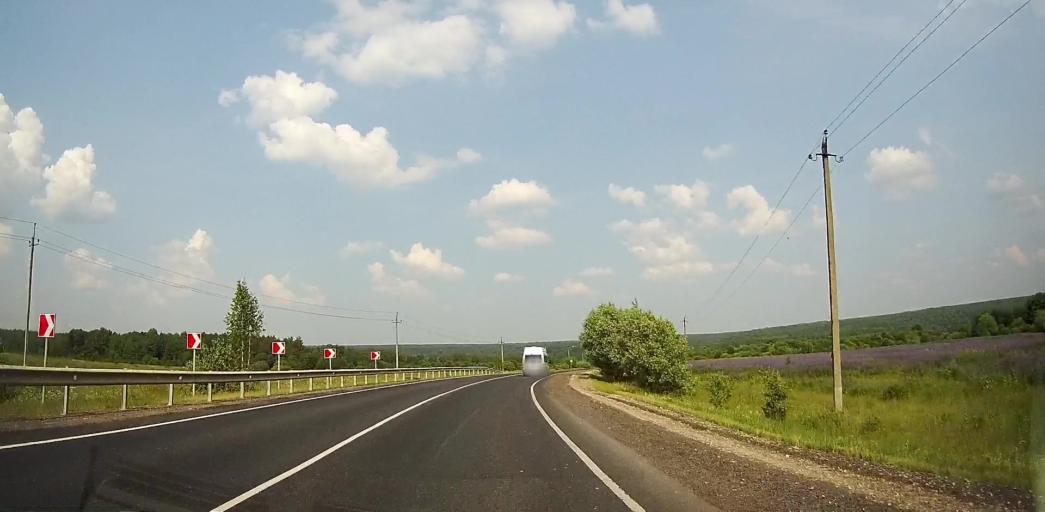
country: RU
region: Moskovskaya
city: Stupino
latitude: 54.9648
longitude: 38.1254
